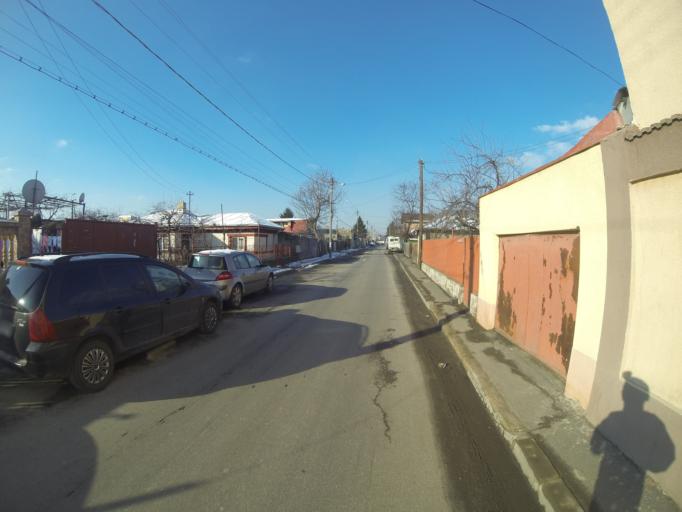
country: RO
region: Bucuresti
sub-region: Municipiul Bucuresti
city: Bucuresti
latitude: 44.3916
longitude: 26.0633
